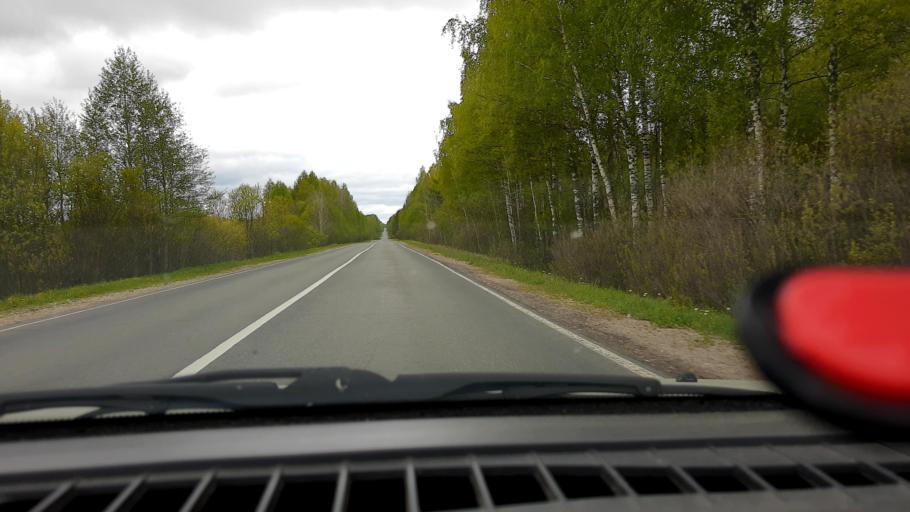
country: RU
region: Nizjnij Novgorod
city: Uren'
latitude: 57.2732
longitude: 45.6294
